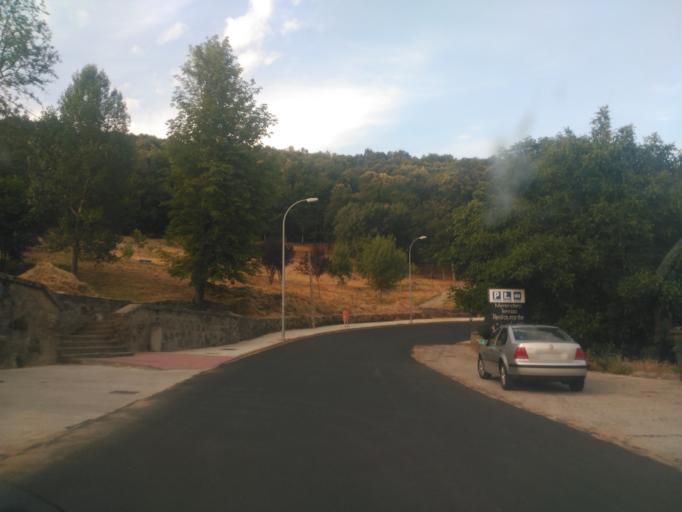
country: ES
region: Castille and Leon
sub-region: Provincia de Salamanca
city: Bejar
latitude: 40.3827
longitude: -5.7658
